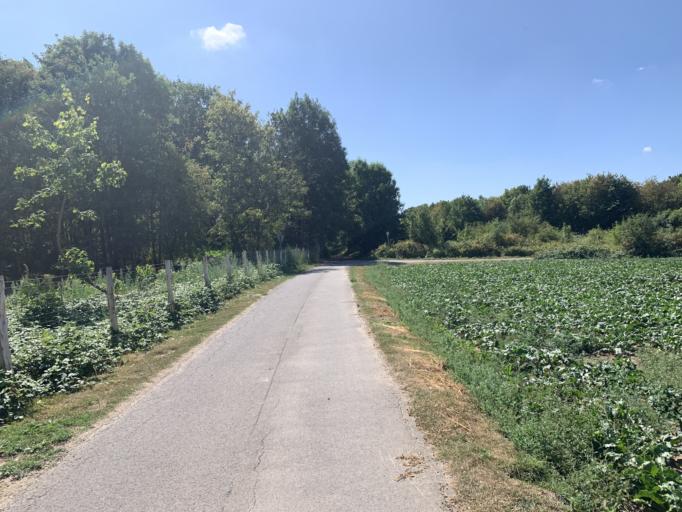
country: DE
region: North Rhine-Westphalia
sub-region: Regierungsbezirk Dusseldorf
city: Meerbusch
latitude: 51.2726
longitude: 6.7267
